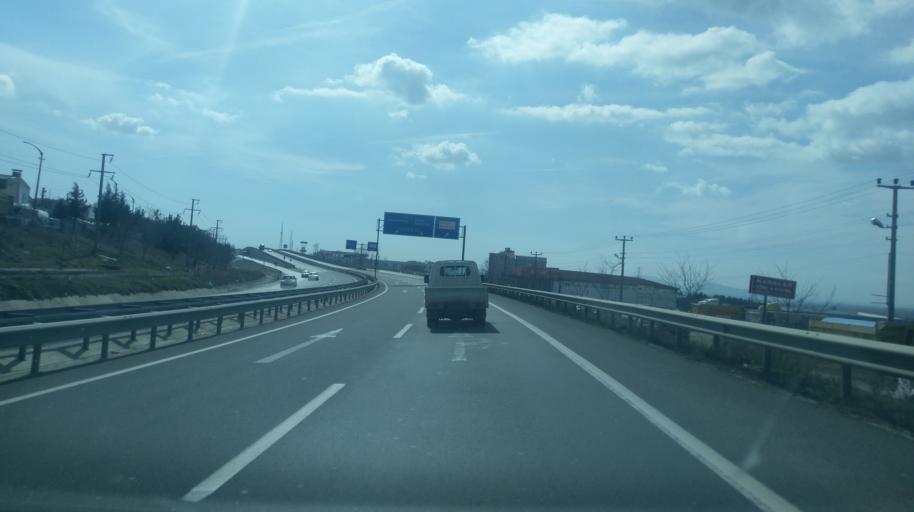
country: TR
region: Edirne
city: Kesan
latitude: 40.8641
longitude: 26.6227
